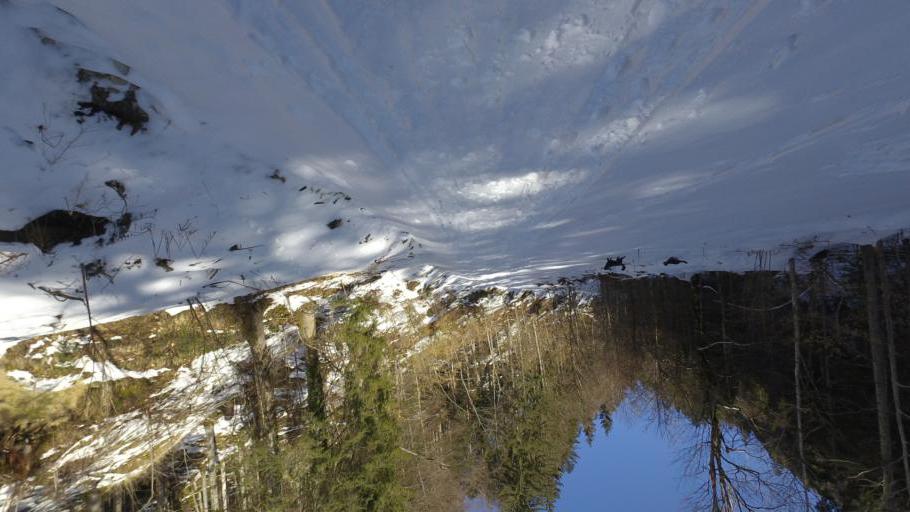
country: DE
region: Bavaria
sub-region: Upper Bavaria
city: Ruhpolding
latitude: 47.7496
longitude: 12.6025
